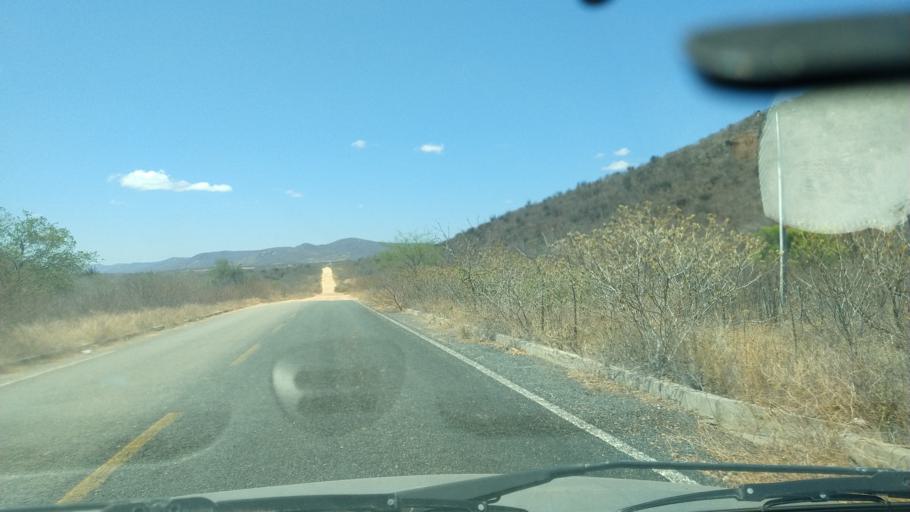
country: BR
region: Rio Grande do Norte
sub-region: Sao Tome
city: Sao Tome
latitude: -5.9686
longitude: -36.1601
